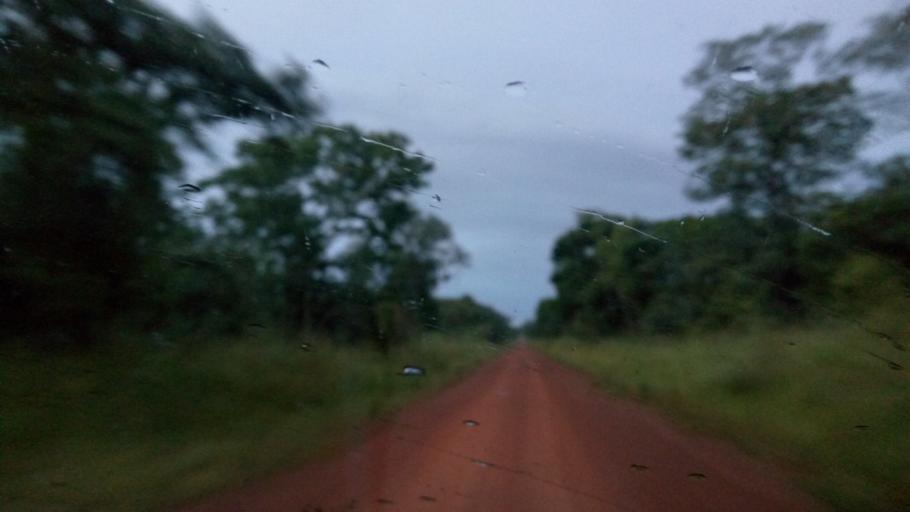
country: ZM
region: Luapula
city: Mwense
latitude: -9.8461
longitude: 28.1245
